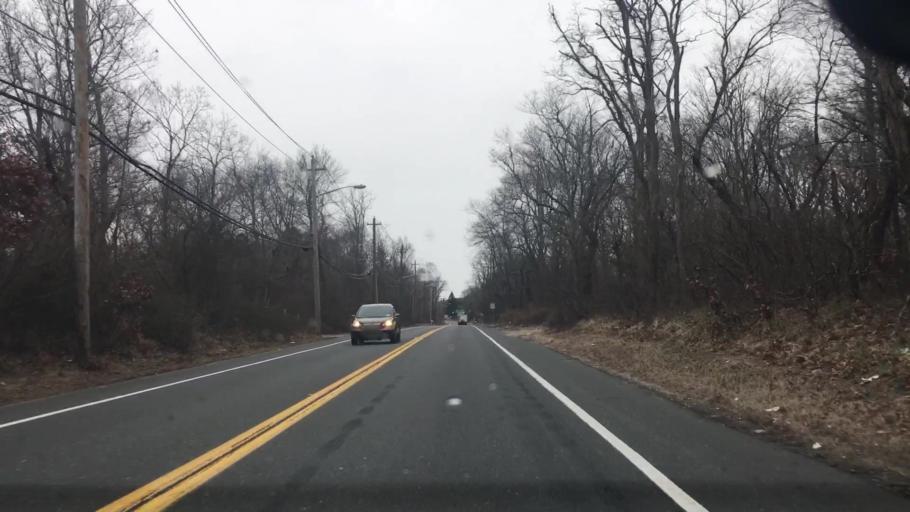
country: US
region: New York
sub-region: Suffolk County
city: Yaphank
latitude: 40.8537
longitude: -72.9381
